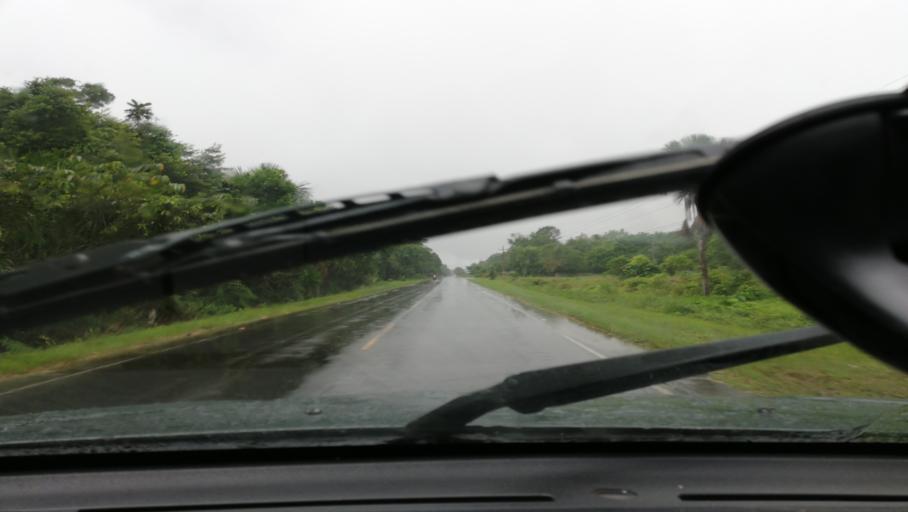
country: PE
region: Loreto
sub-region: Provincia de Maynas
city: San Juan
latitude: -3.9547
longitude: -73.4078
